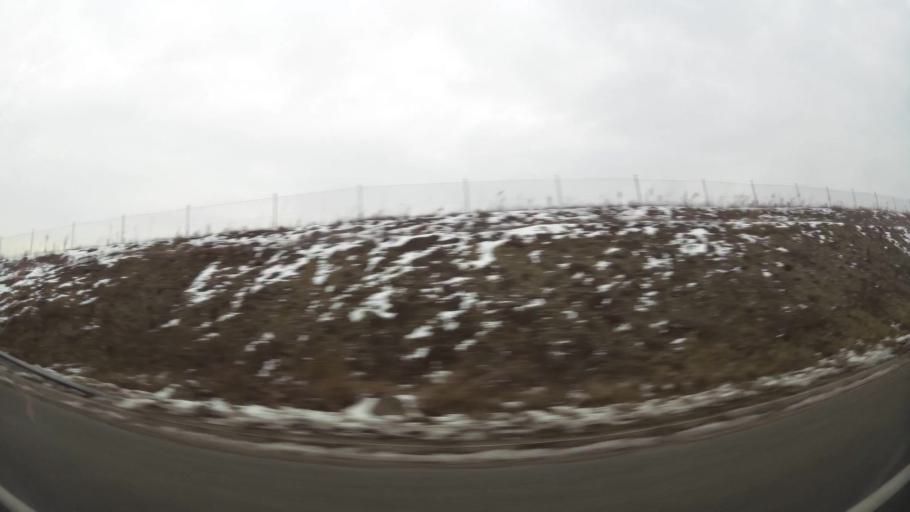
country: MK
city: Kondovo
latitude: 42.0211
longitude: 21.3310
